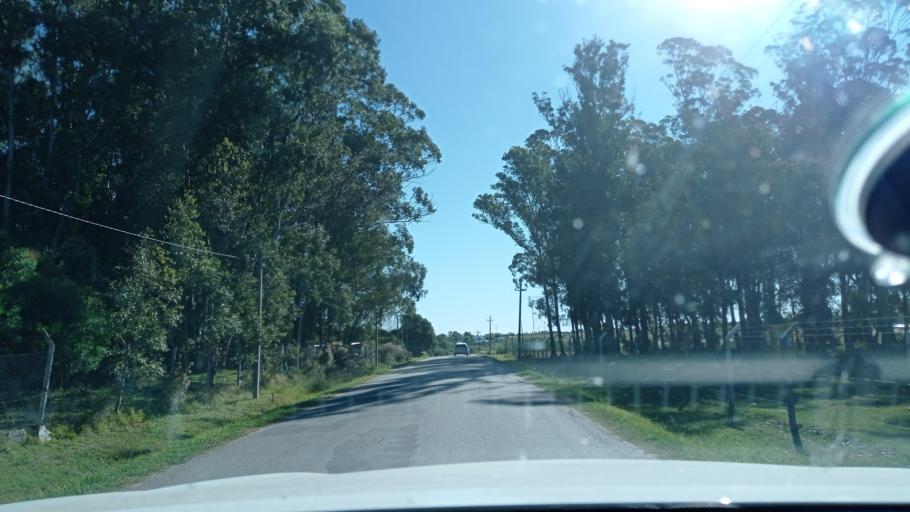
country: UY
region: Canelones
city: Pando
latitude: -34.7578
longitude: -55.9839
